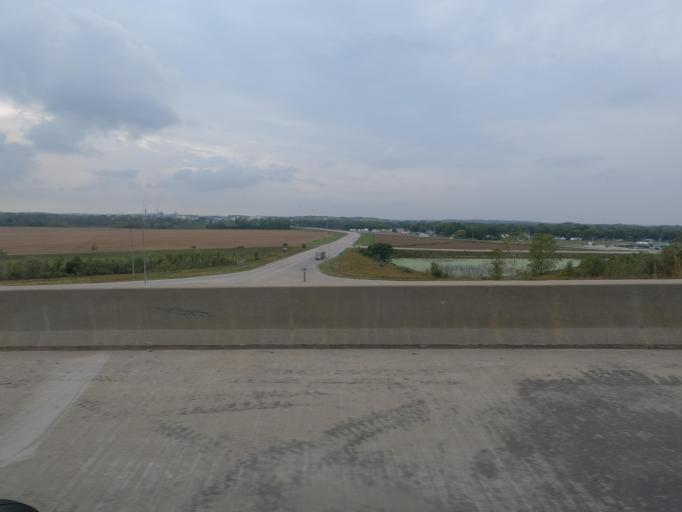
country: US
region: Iowa
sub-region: Wapello County
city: Eddyville
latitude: 41.1513
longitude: -92.6242
